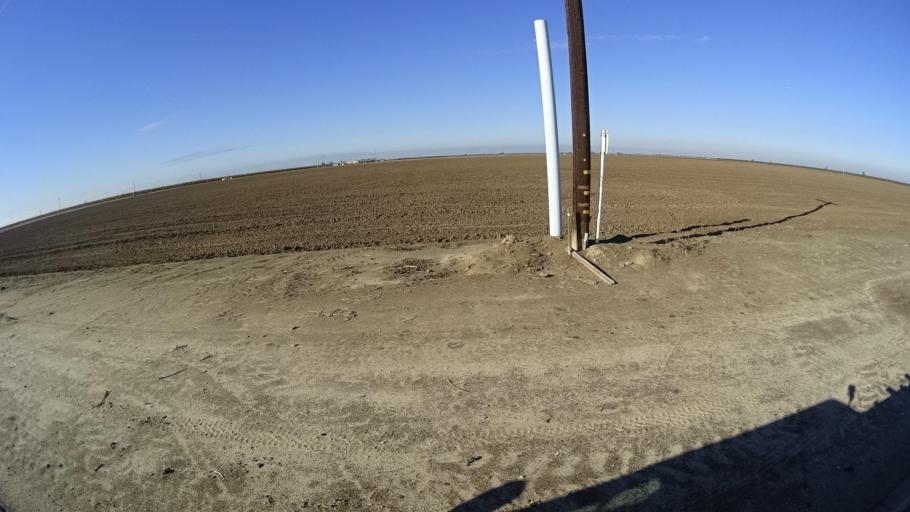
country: US
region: California
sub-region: Kern County
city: McFarland
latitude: 35.7056
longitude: -119.2764
